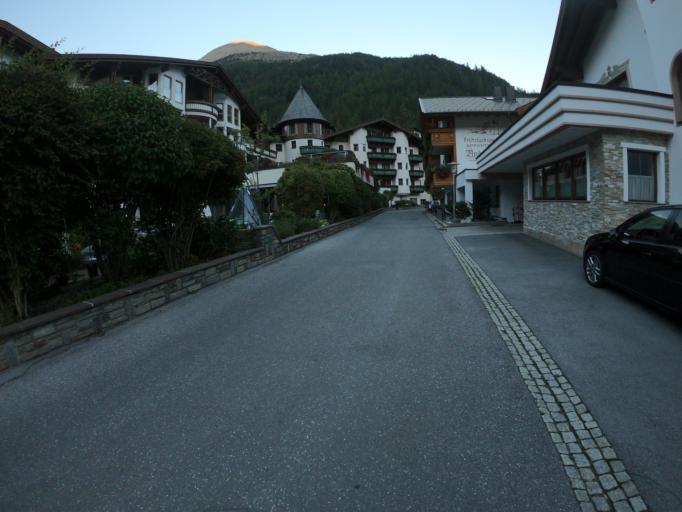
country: AT
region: Tyrol
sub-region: Politischer Bezirk Imst
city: Soelden
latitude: 46.9665
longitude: 11.0087
